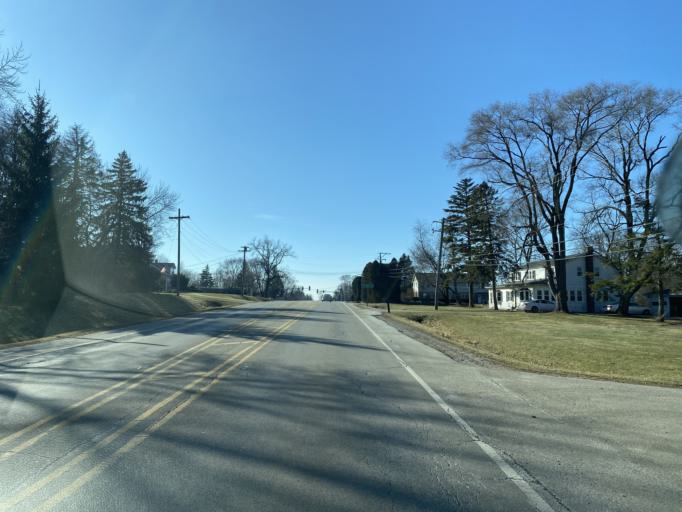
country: US
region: Illinois
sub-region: Will County
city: Lockport
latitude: 41.6140
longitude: -88.0384
